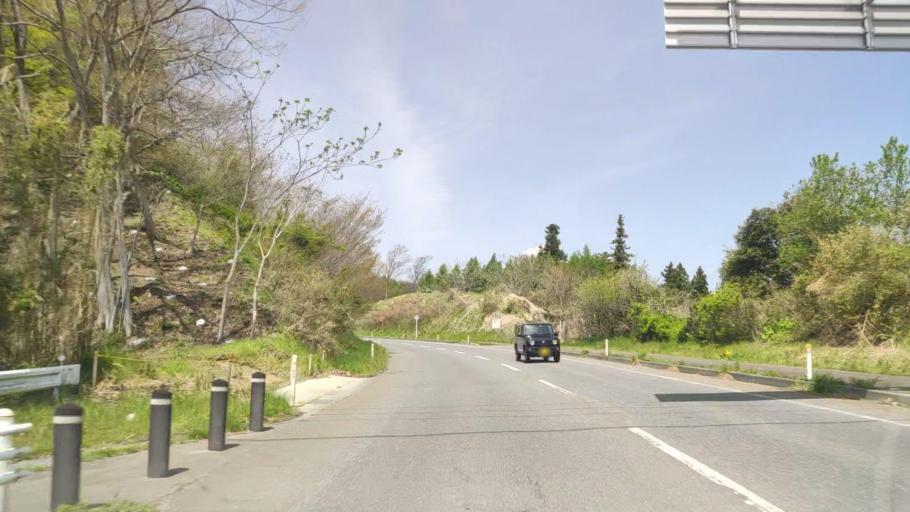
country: JP
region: Aomori
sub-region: Hachinohe Shi
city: Uchimaru
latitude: 40.5198
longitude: 141.4263
